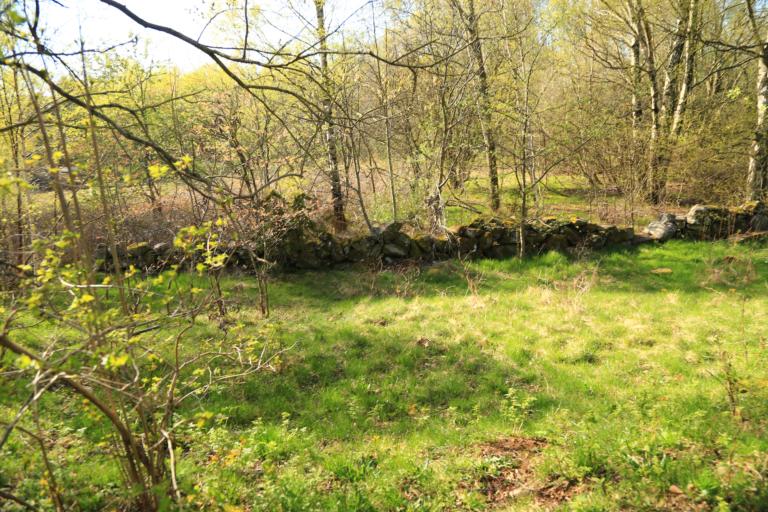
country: SE
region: Halland
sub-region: Varbergs Kommun
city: Varberg
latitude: 57.0883
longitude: 12.2650
